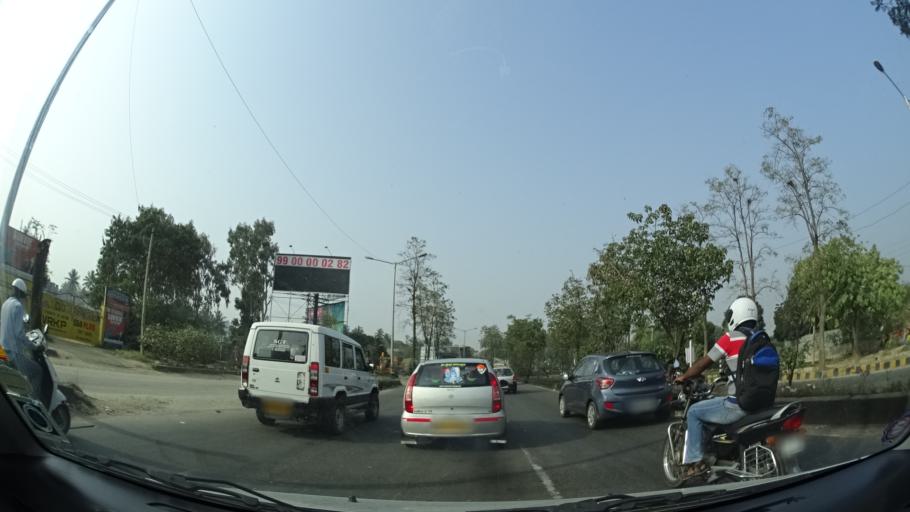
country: IN
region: Karnataka
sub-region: Bangalore Urban
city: Yelahanka
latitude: 13.0423
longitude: 77.5980
